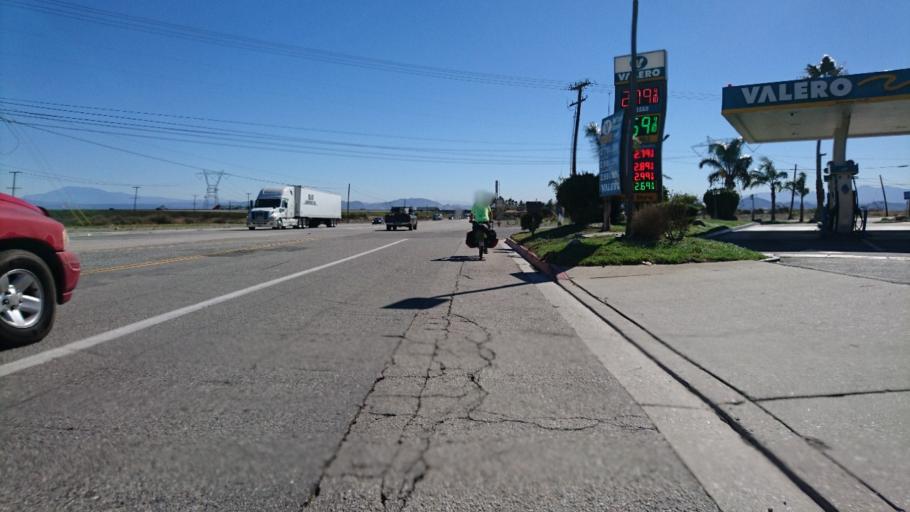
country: US
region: California
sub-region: San Bernardino County
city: Fontana
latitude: 34.1861
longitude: -117.4393
